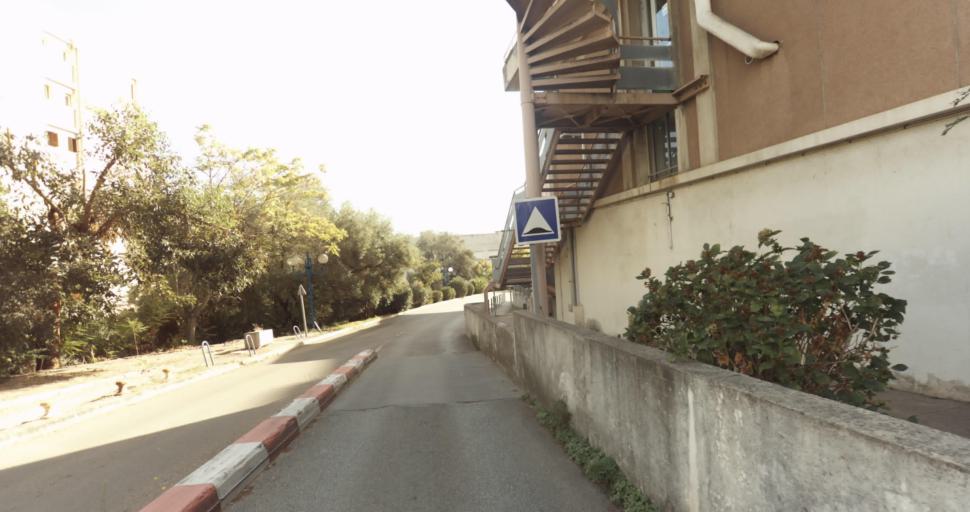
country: FR
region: Corsica
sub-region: Departement de la Corse-du-Sud
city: Ajaccio
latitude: 41.9234
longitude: 8.7339
